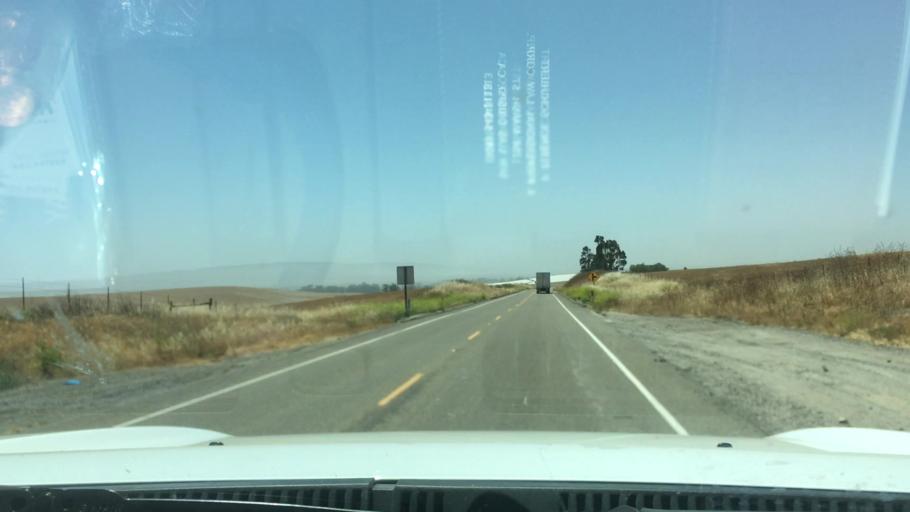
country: US
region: California
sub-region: Santa Barbara County
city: Santa Maria
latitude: 34.9965
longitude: -120.4114
